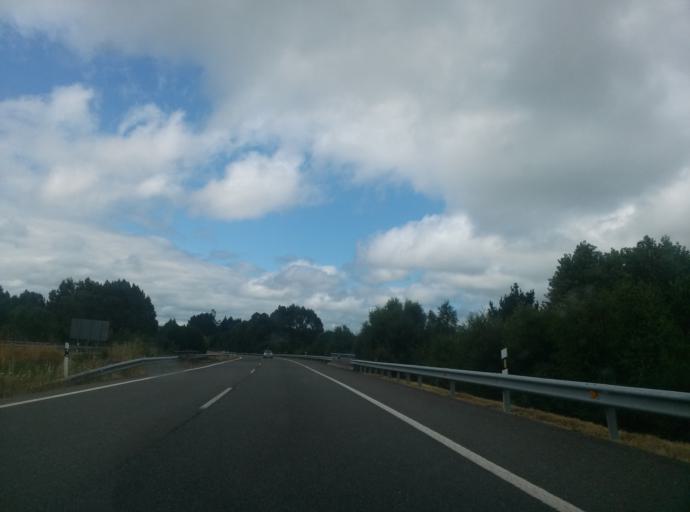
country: ES
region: Galicia
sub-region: Provincia de Lugo
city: Rabade
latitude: 43.1134
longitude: -7.6052
